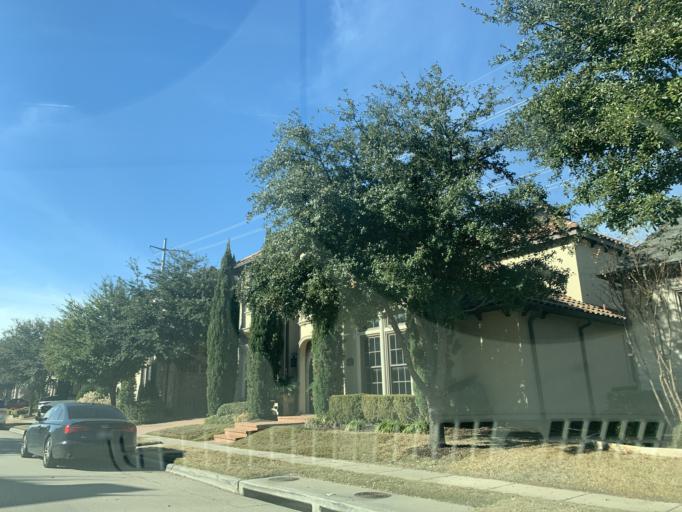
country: US
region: Texas
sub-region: Denton County
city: The Colony
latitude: 33.0598
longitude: -96.8193
